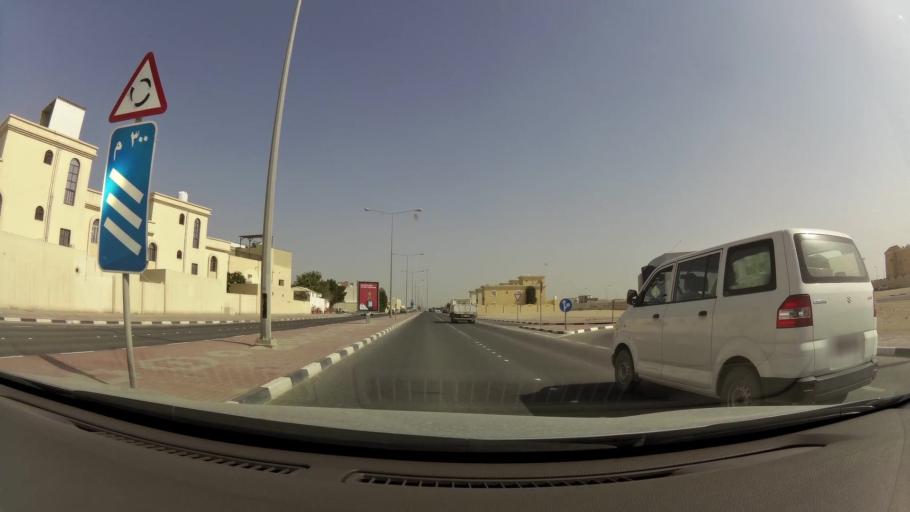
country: QA
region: Baladiyat ar Rayyan
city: Ar Rayyan
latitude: 25.3475
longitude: 51.4443
